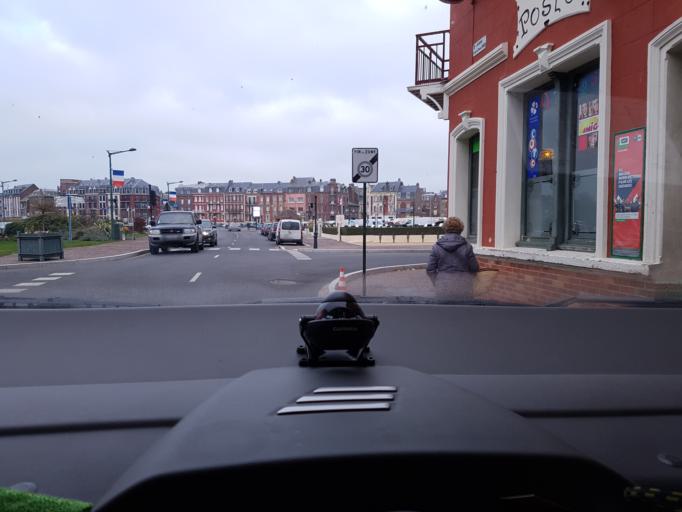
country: FR
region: Picardie
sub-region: Departement de la Somme
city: Mers-les-Bains
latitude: 50.0660
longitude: 1.3877
